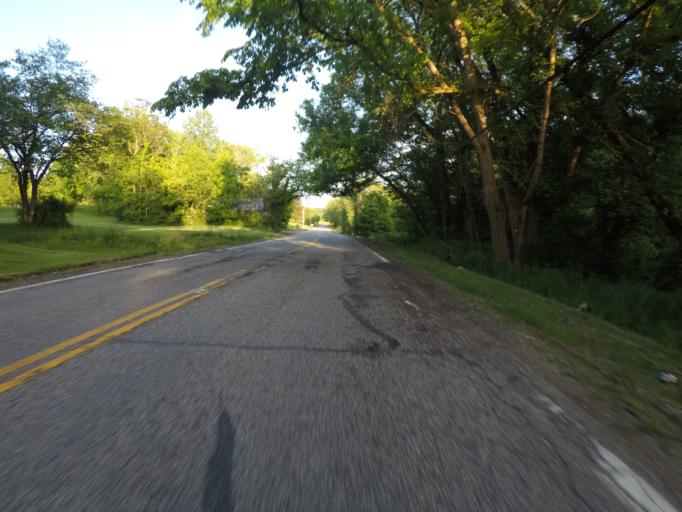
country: US
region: West Virginia
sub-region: Cabell County
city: Huntington
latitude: 38.4888
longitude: -82.4741
